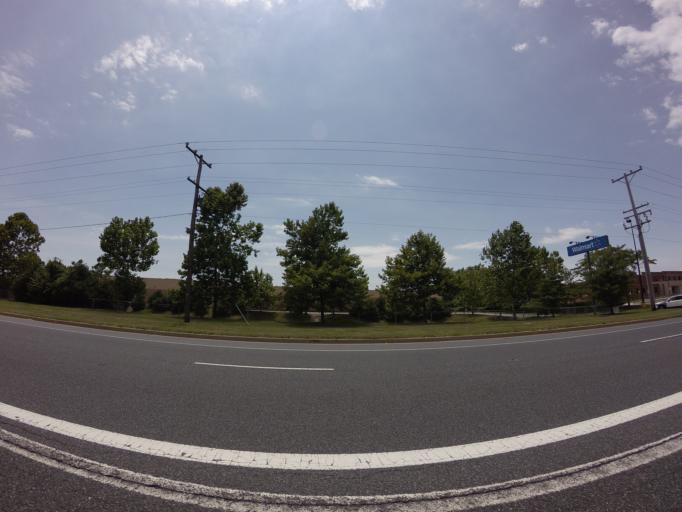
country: US
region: Maryland
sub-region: Baltimore County
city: Essex
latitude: 39.2864
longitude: -76.4974
